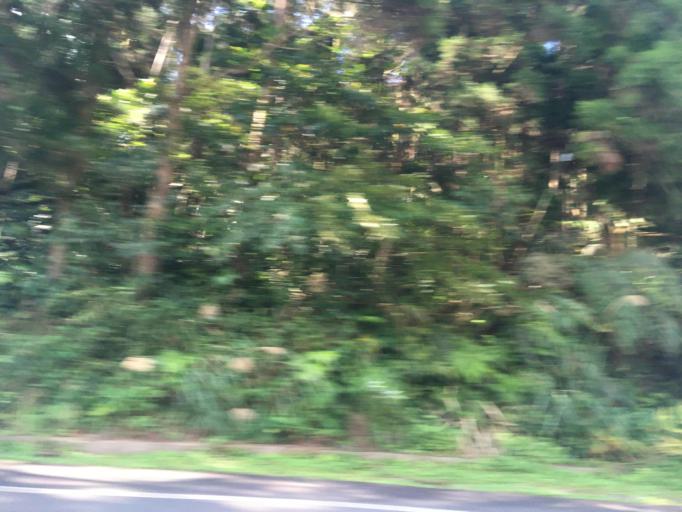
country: TW
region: Taiwan
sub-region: Yilan
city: Yilan
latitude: 24.7533
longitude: 121.6316
